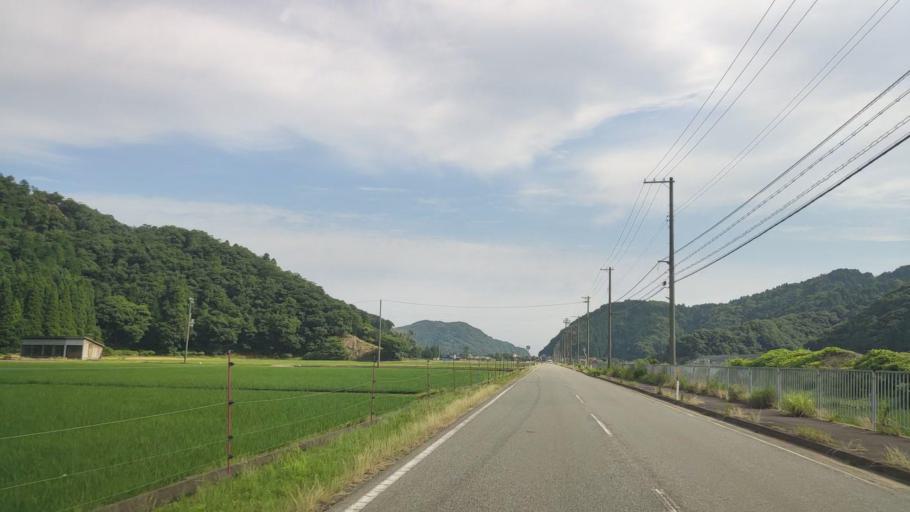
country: JP
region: Hyogo
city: Toyooka
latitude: 35.6266
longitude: 134.8411
